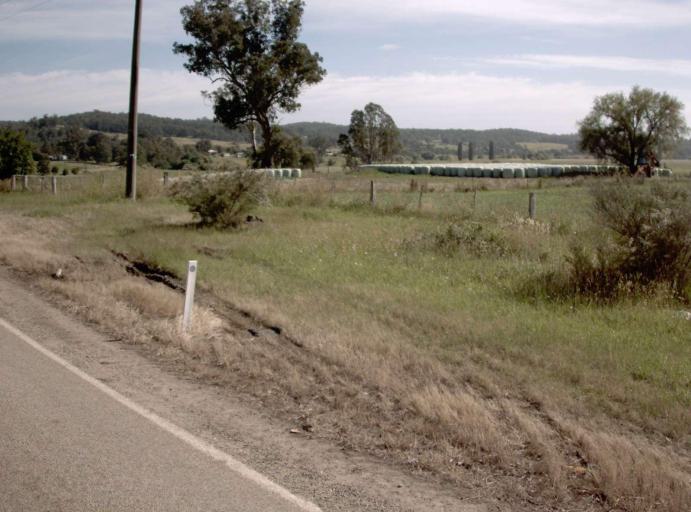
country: AU
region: Victoria
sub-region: East Gippsland
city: Bairnsdale
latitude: -37.7226
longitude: 147.8061
